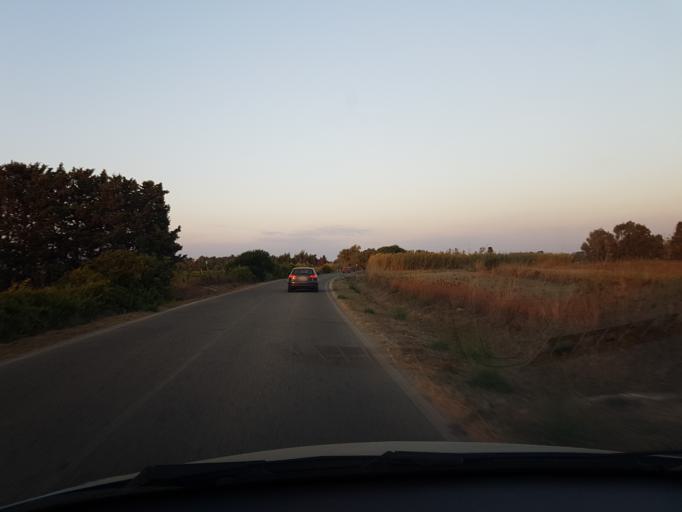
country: IT
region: Sardinia
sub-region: Provincia di Oristano
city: Riola Sardo
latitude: 39.9941
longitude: 8.4713
